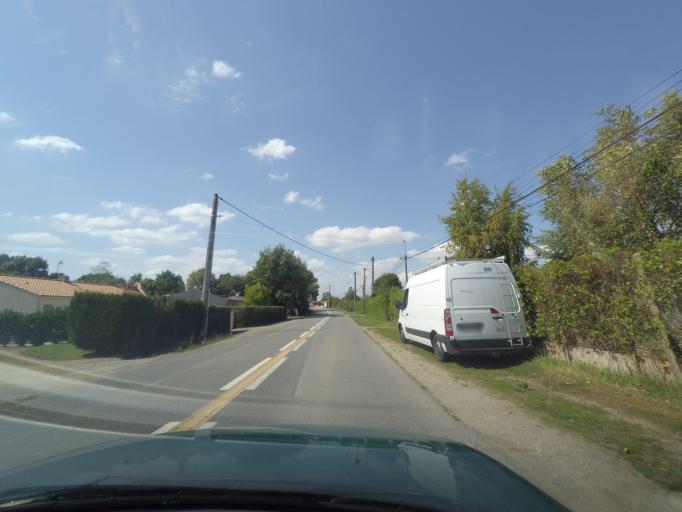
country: FR
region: Pays de la Loire
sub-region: Departement de la Loire-Atlantique
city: Sainte-Pazanne
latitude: 47.0758
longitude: -1.7834
